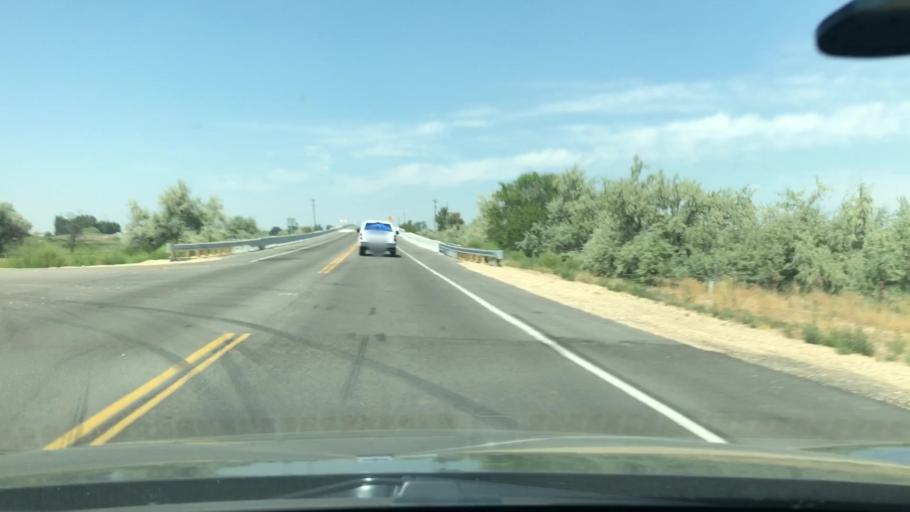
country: US
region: Idaho
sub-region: Canyon County
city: Parma
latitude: 43.7624
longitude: -116.9118
